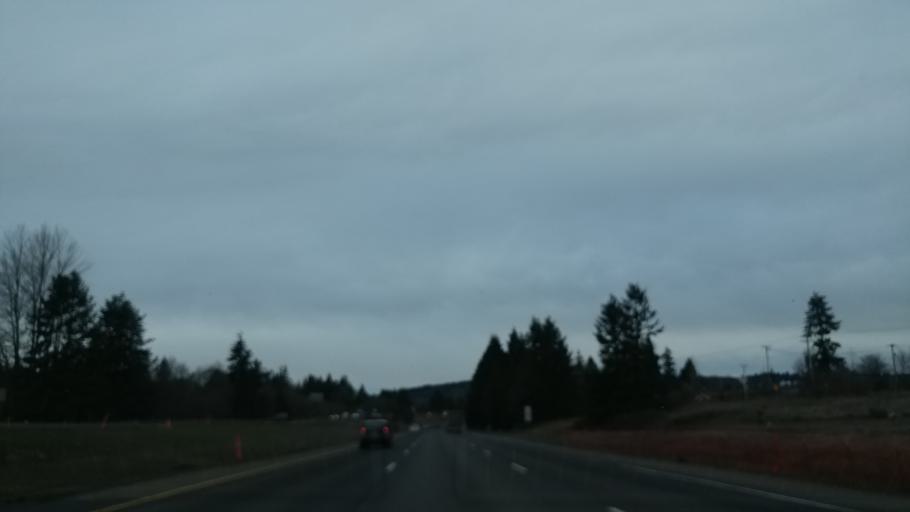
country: US
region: Washington
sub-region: Clark County
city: La Center
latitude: 45.8535
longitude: -122.7033
